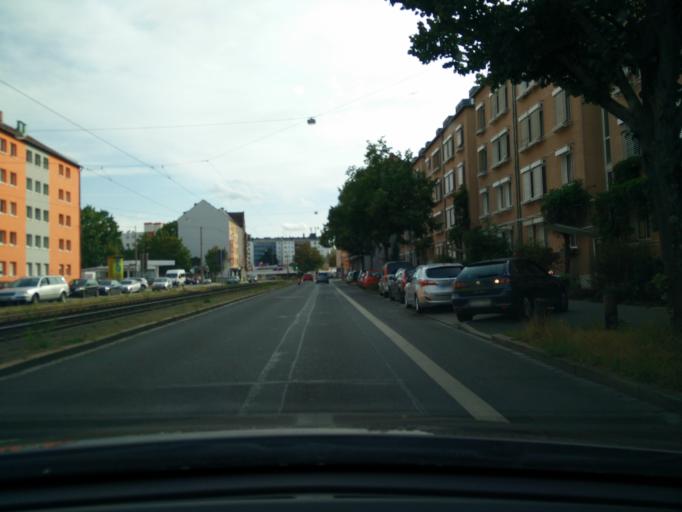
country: DE
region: Bavaria
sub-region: Regierungsbezirk Mittelfranken
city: Nuernberg
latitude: 49.4307
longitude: 11.0663
